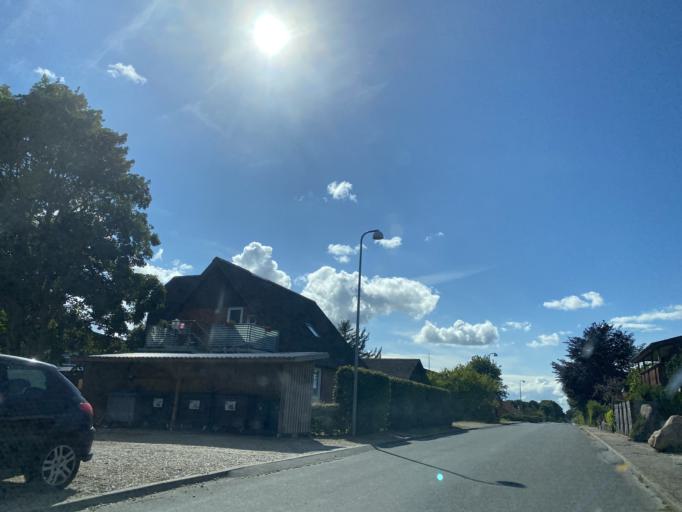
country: DK
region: Central Jutland
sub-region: Favrskov Kommune
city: Hammel
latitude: 56.2647
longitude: 9.7313
